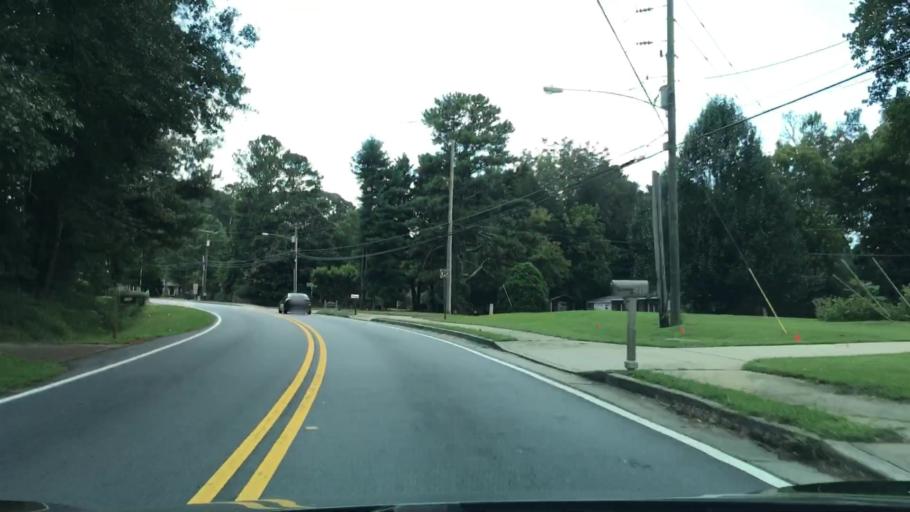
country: US
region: Georgia
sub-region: Gwinnett County
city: Snellville
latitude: 33.8945
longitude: -84.0685
